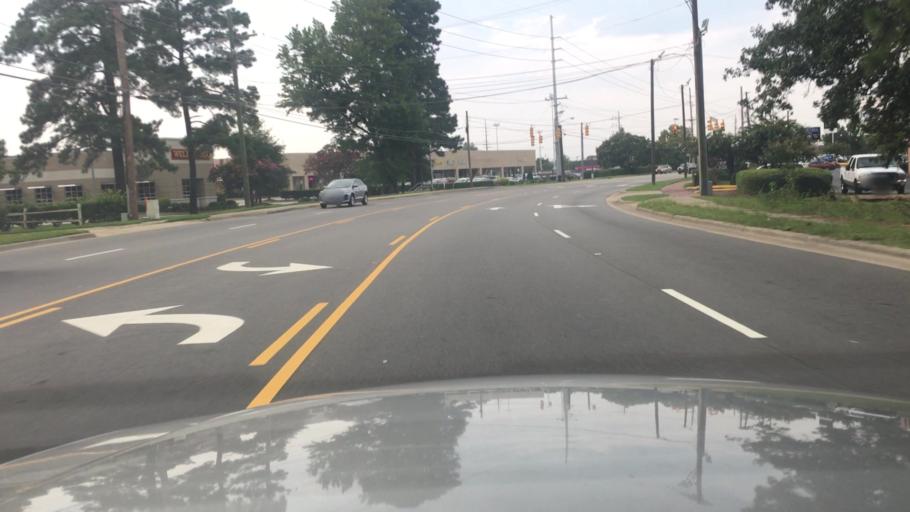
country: US
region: North Carolina
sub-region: Cumberland County
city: Fayetteville
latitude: 35.0641
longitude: -78.9507
